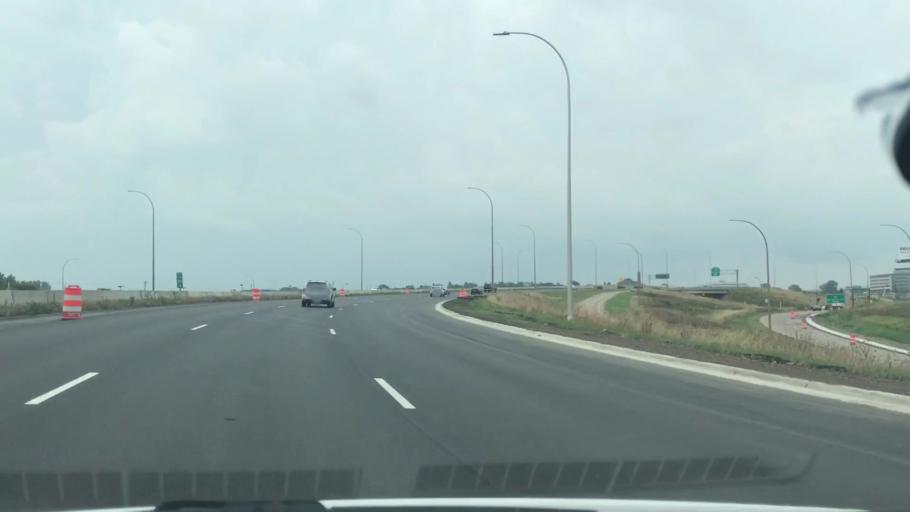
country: US
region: Minnesota
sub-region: Hennepin County
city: Saint Anthony
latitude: 45.0016
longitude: -93.2346
